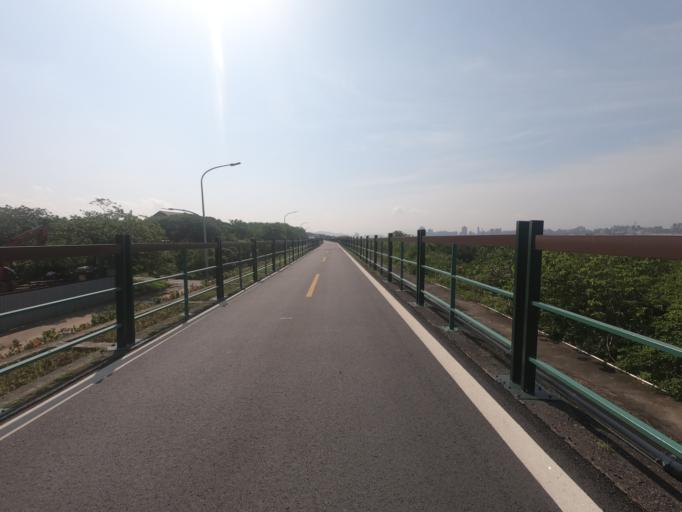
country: TW
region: Taipei
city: Taipei
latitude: 25.1086
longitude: 121.4668
